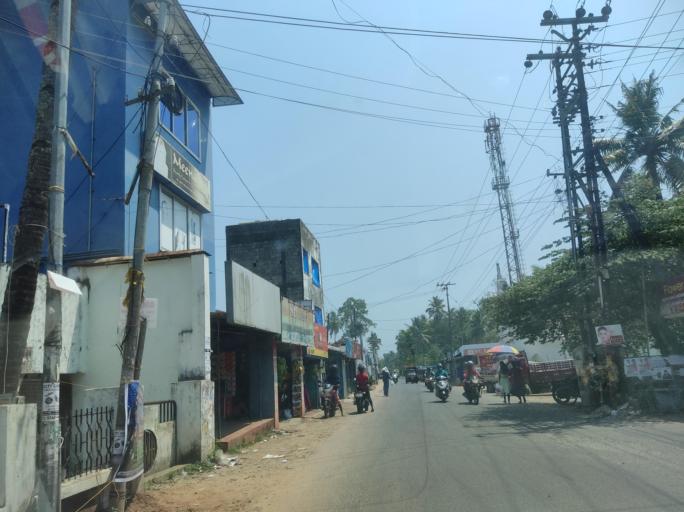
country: IN
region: Kerala
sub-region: Alappuzha
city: Kutiatodu
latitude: 9.8223
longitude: 76.2985
